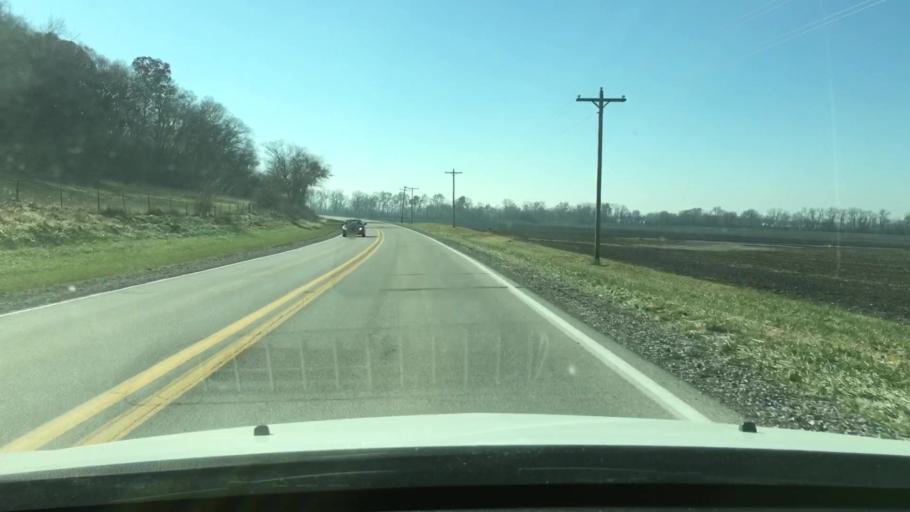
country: US
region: Illinois
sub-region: Morgan County
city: Meredosia
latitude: 39.7267
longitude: -90.5667
